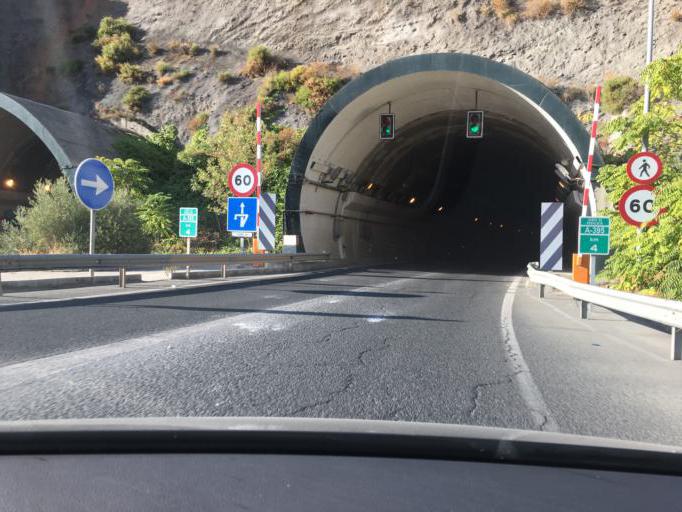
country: ES
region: Andalusia
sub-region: Provincia de Granada
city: Huetor Vega
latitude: 37.1610
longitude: -3.5726
